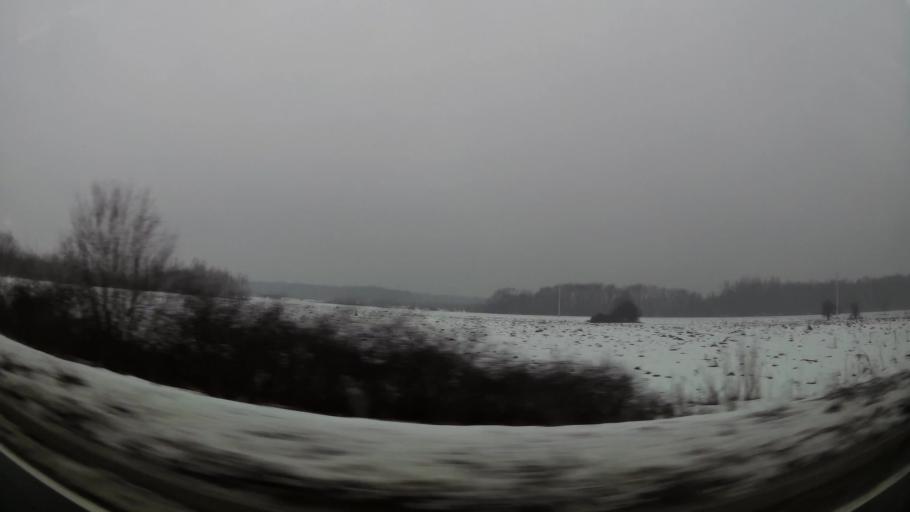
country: RS
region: Central Serbia
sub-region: Belgrade
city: Cukarica
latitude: 44.7710
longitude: 20.3952
